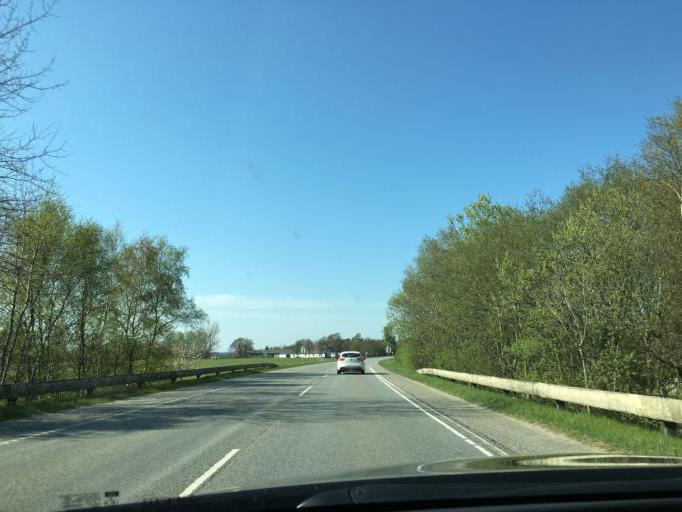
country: DK
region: South Denmark
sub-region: Kolding Kommune
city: Kolding
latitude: 55.5525
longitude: 9.4422
